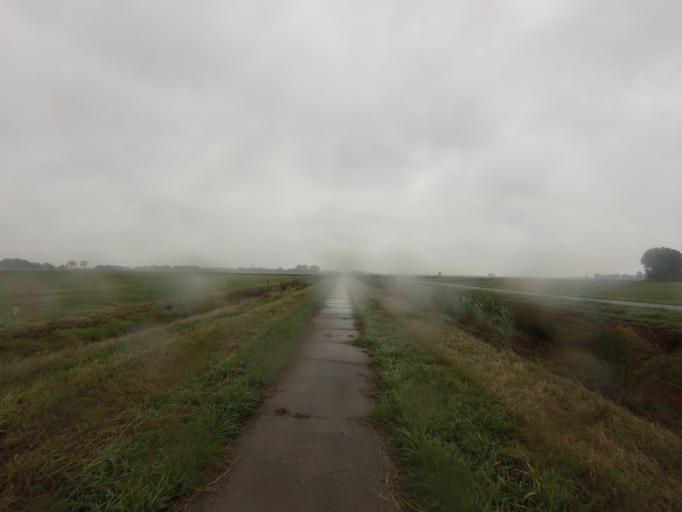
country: NL
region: Friesland
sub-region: Gemeente Boarnsterhim
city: Aldeboarn
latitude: 53.0351
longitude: 5.8864
